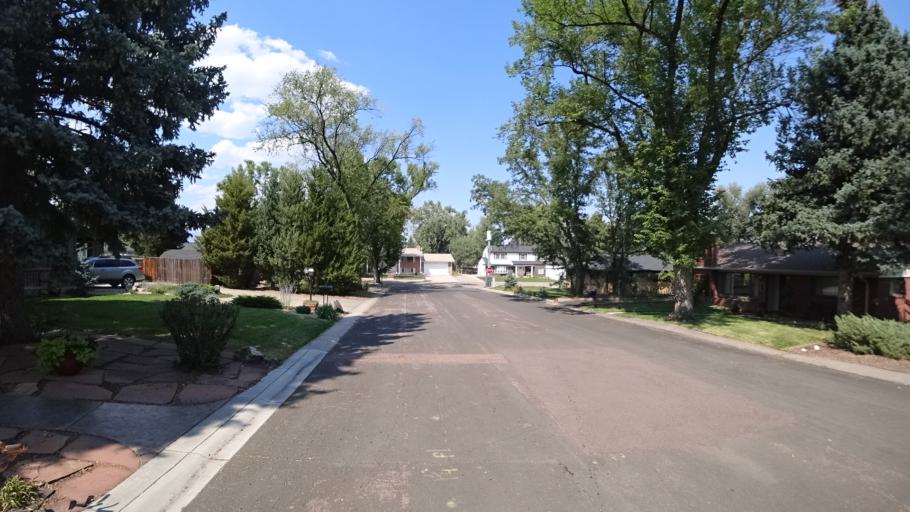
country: US
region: Colorado
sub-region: El Paso County
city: Colorado Springs
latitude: 38.8005
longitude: -104.8312
